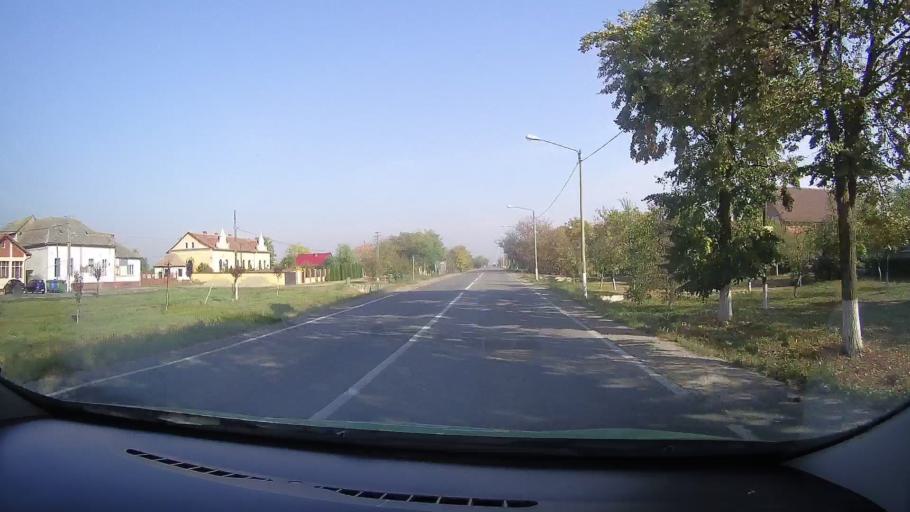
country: RO
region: Arad
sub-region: Comuna Pilu
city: Pilu
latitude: 46.5765
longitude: 21.3428
